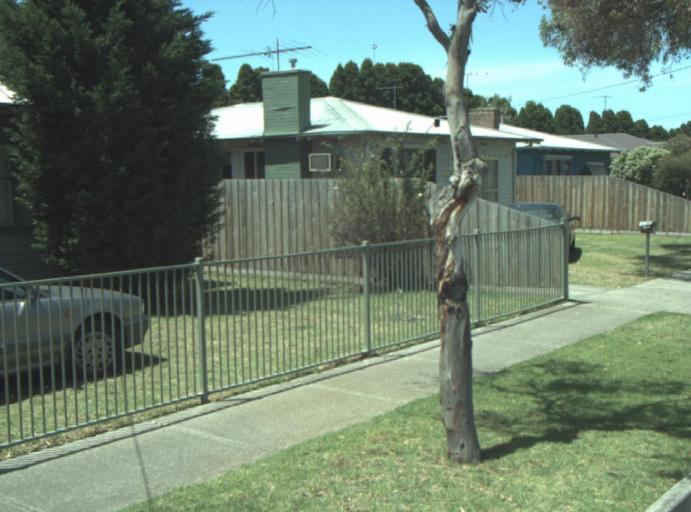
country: AU
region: Victoria
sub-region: Greater Geelong
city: Bell Park
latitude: -38.0907
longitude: 144.3484
